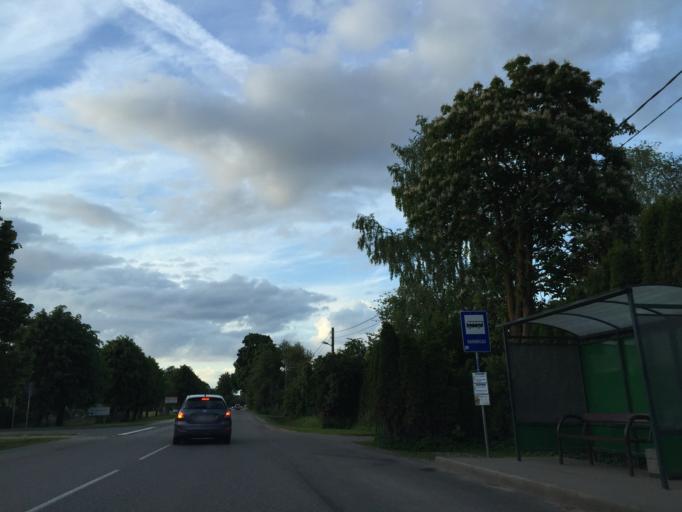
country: LV
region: Babite
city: Pinki
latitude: 56.9523
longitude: 23.9134
